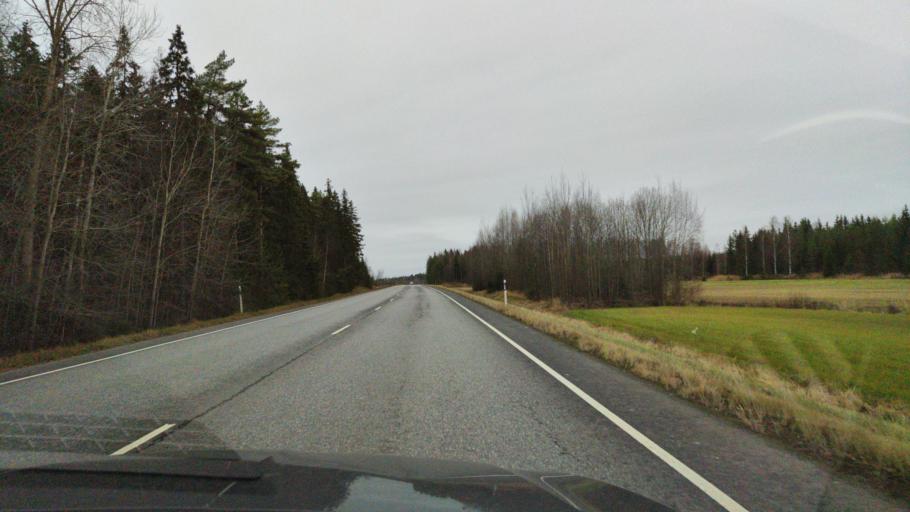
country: FI
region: Satakunta
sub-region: Rauma
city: Saekylae
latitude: 61.0041
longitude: 22.4103
